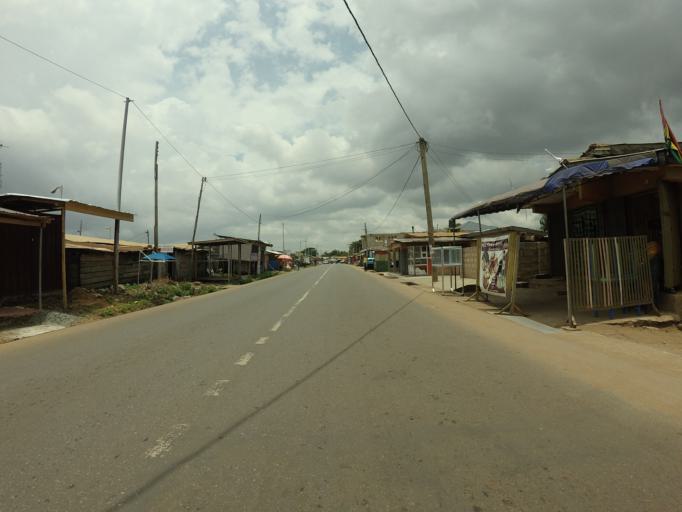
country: GH
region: Greater Accra
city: Medina Estates
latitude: 5.6789
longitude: -0.1495
